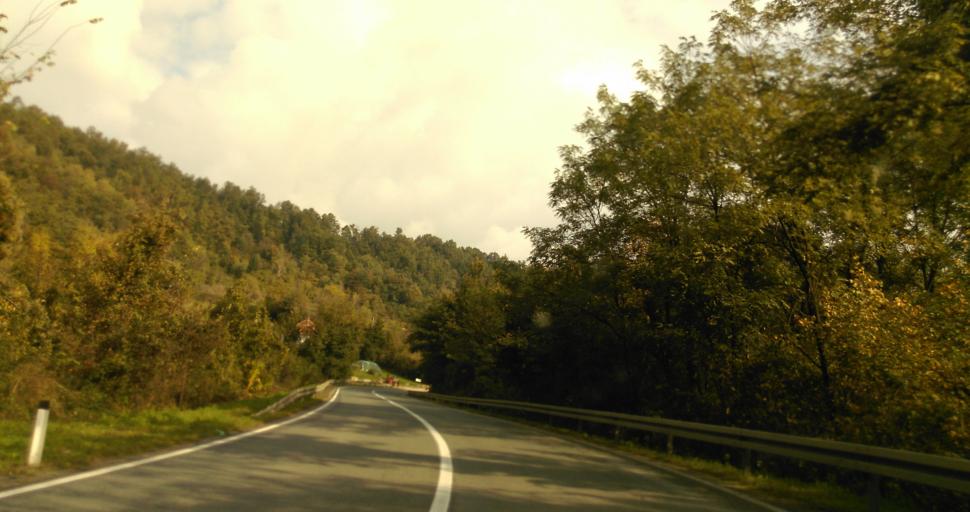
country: RS
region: Central Serbia
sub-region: Kolubarski Okrug
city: Ljig
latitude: 44.2011
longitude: 20.2439
